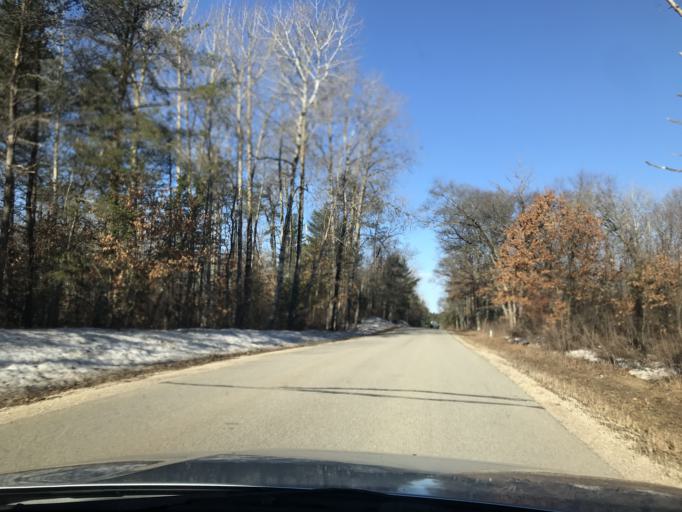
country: US
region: Wisconsin
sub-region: Marinette County
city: Niagara
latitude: 45.3981
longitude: -88.0823
